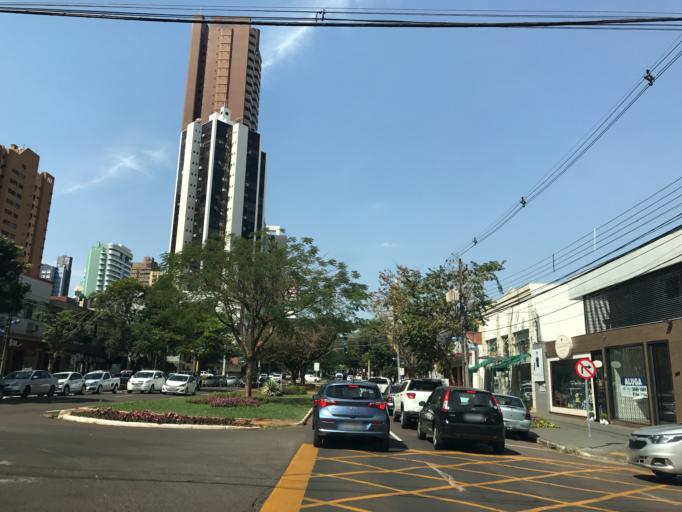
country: BR
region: Parana
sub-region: Maringa
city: Maringa
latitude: -23.4256
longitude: -51.9446
